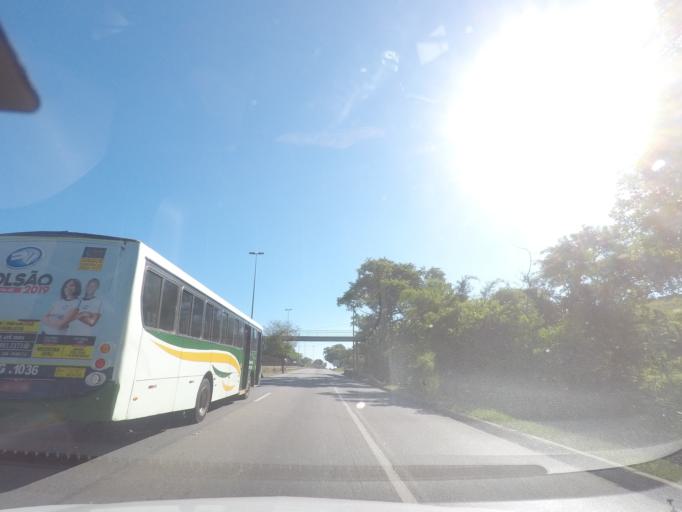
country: BR
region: Rio de Janeiro
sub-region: Guapimirim
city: Guapimirim
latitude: -22.6619
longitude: -43.0936
